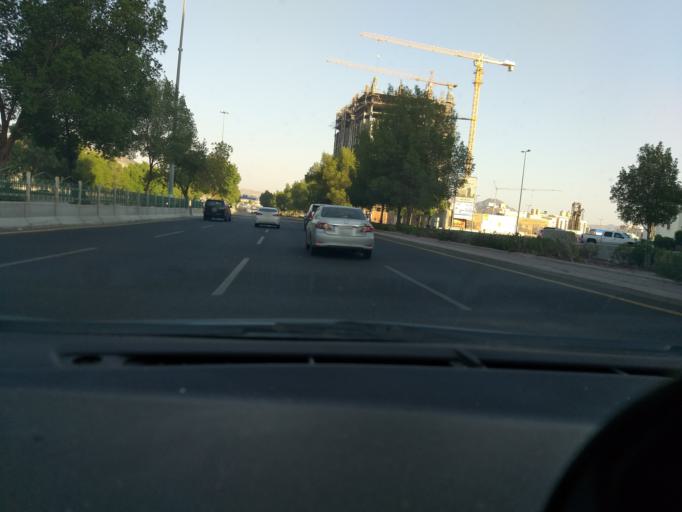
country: SA
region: Makkah
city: Mecca
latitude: 21.3749
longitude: 39.8790
